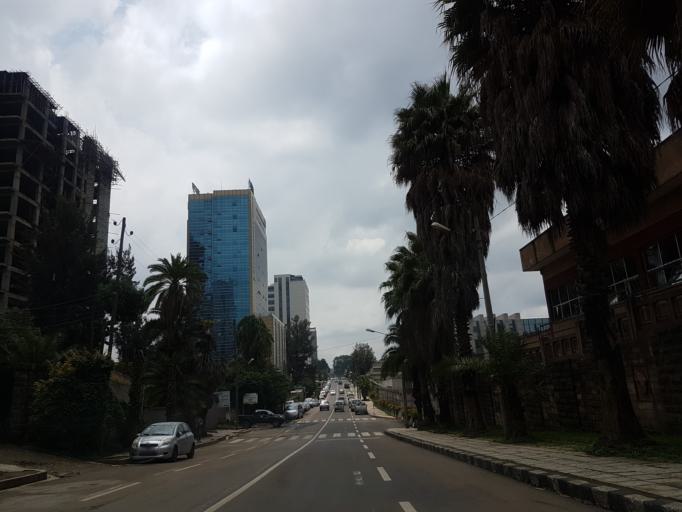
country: ET
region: Adis Abeba
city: Addis Ababa
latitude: 9.0024
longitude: 38.7428
